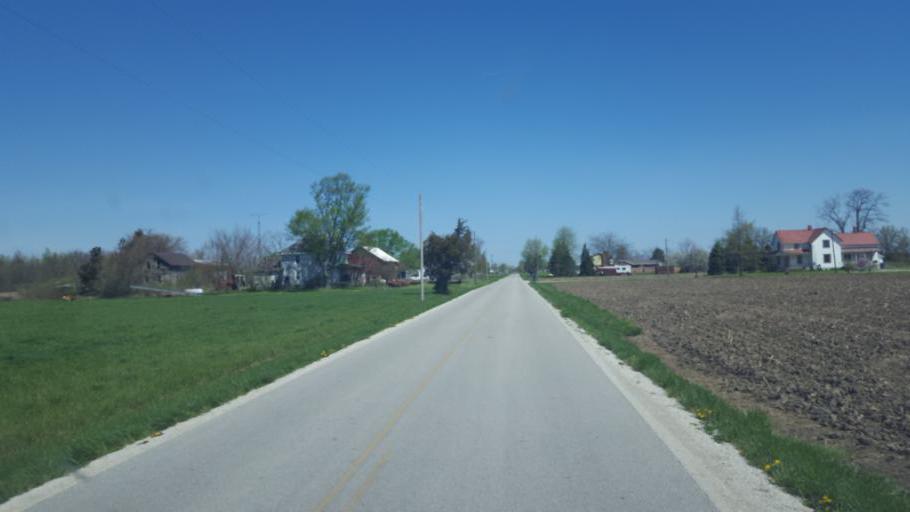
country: US
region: Ohio
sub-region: Ottawa County
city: Oak Harbor
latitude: 41.4794
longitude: -83.1259
